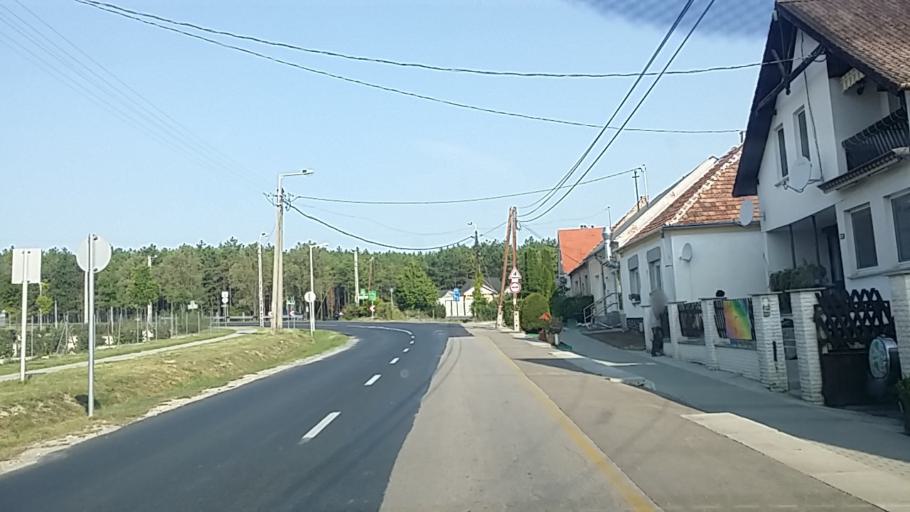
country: HU
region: Gyor-Moson-Sopron
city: Fertorakos
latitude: 47.7272
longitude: 16.6441
